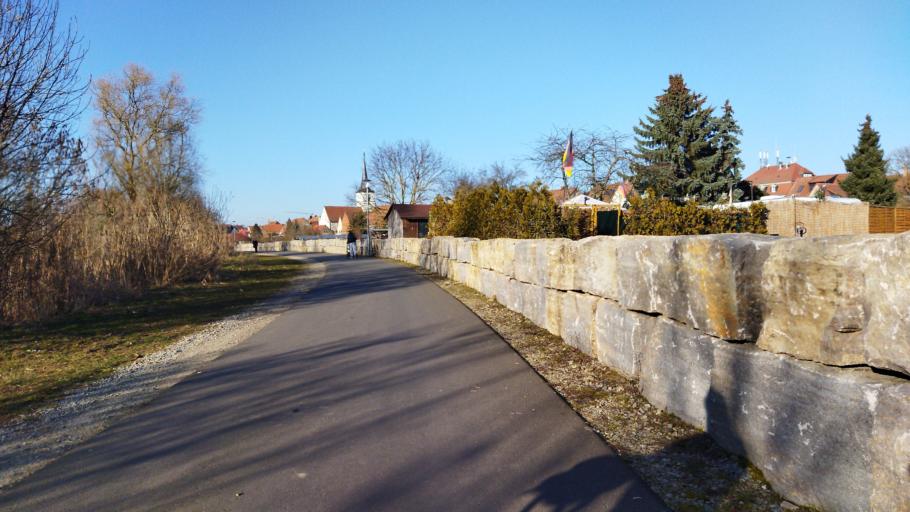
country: DE
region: Bavaria
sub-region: Regierungsbezirk Unterfranken
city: Albertshofen
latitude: 49.7683
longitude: 10.1580
